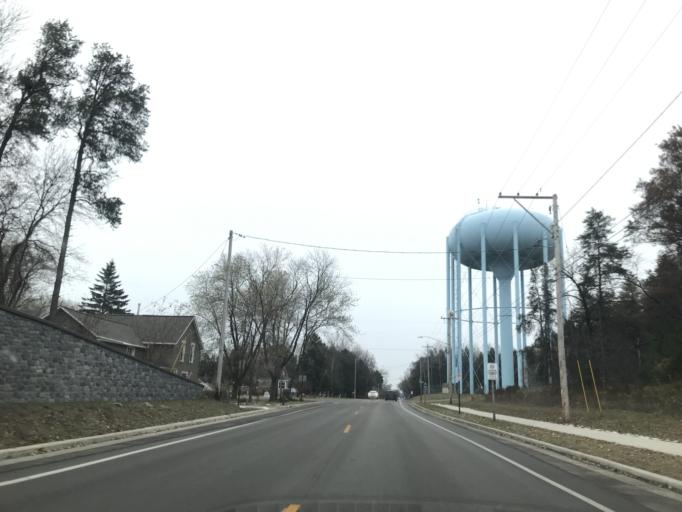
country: US
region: Wisconsin
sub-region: Marinette County
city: Marinette
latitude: 45.0787
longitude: -87.6296
